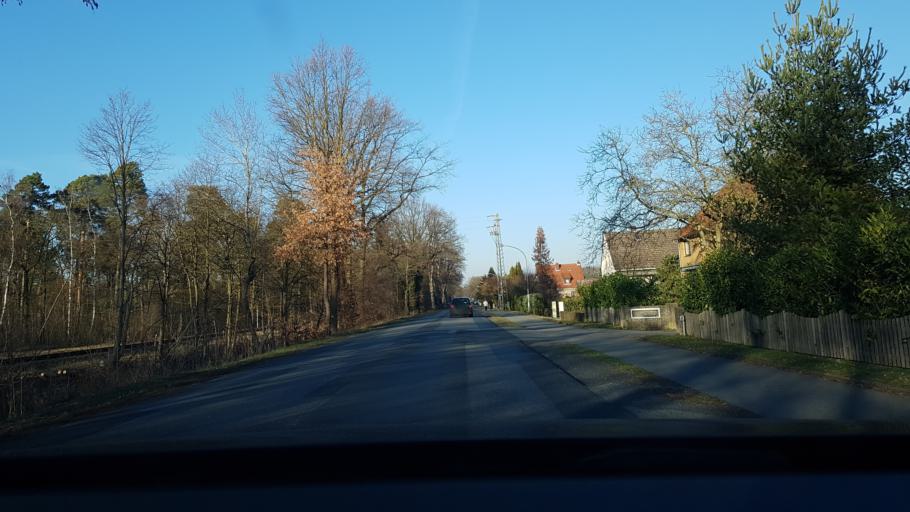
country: DE
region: Lower Saxony
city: Gifhorn
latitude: 52.5028
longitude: 10.5740
